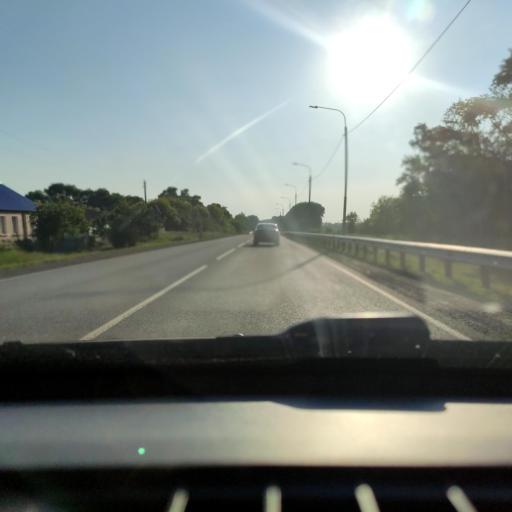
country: RU
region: Voronezj
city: Kashirskoye
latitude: 51.4582
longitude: 39.8099
